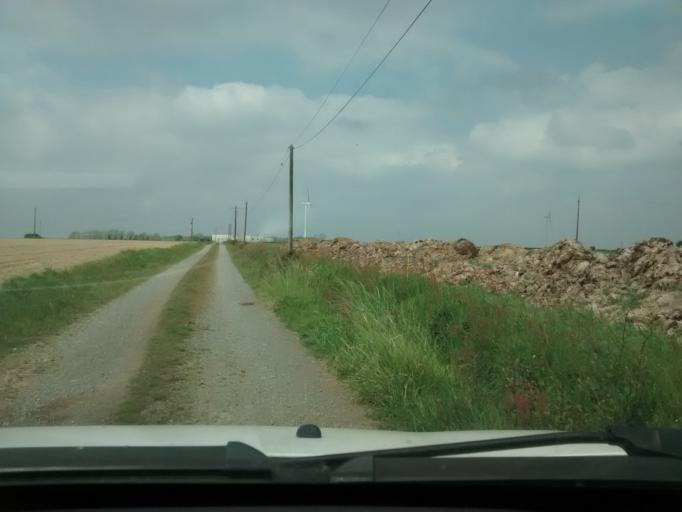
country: FR
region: Brittany
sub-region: Departement d'Ille-et-Vilaine
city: Grand-Fougeray
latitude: 47.7716
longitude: -1.7461
